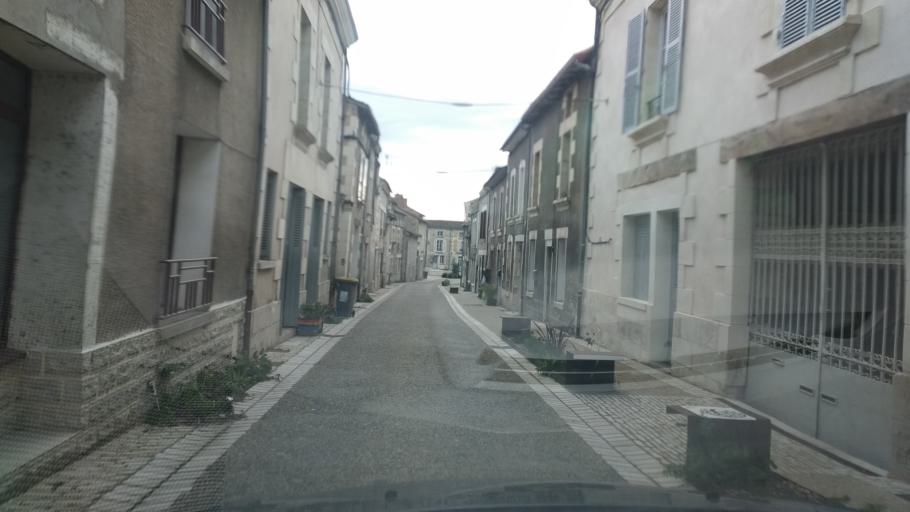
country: FR
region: Poitou-Charentes
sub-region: Departement de la Vienne
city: Dissay
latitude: 46.6999
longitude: 0.4303
